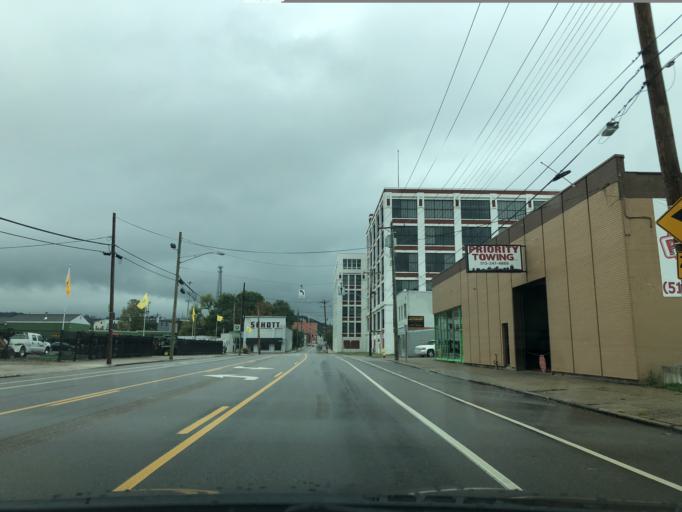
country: US
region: Ohio
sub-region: Hamilton County
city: Saint Bernard
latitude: 39.1599
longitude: -84.5354
